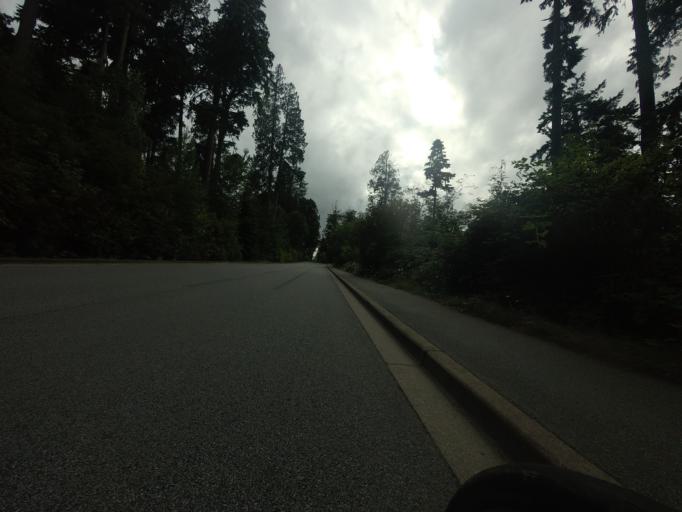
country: CA
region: British Columbia
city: West End
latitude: 49.3114
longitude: -123.1474
